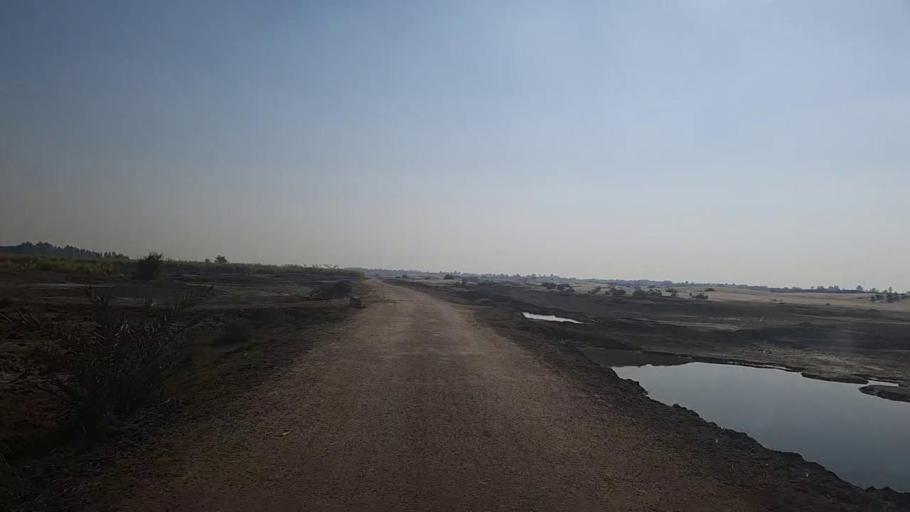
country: PK
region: Sindh
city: Khairpur
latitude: 27.4384
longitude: 68.7278
